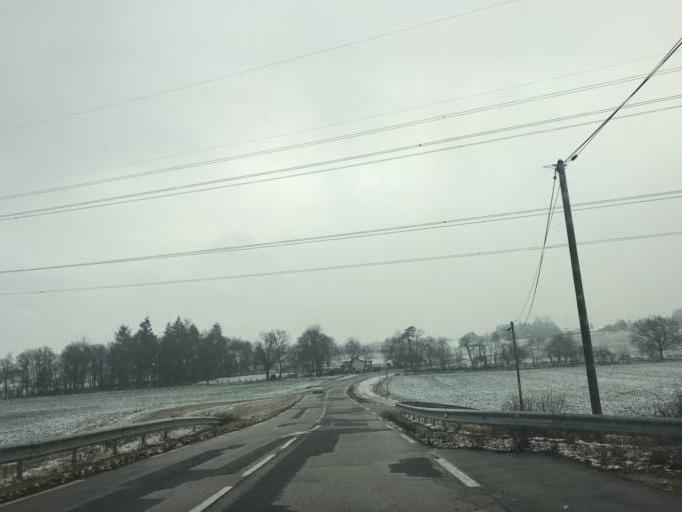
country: FR
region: Rhone-Alpes
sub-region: Departement de l'Ain
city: Tramoyes
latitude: 45.8605
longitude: 4.9595
